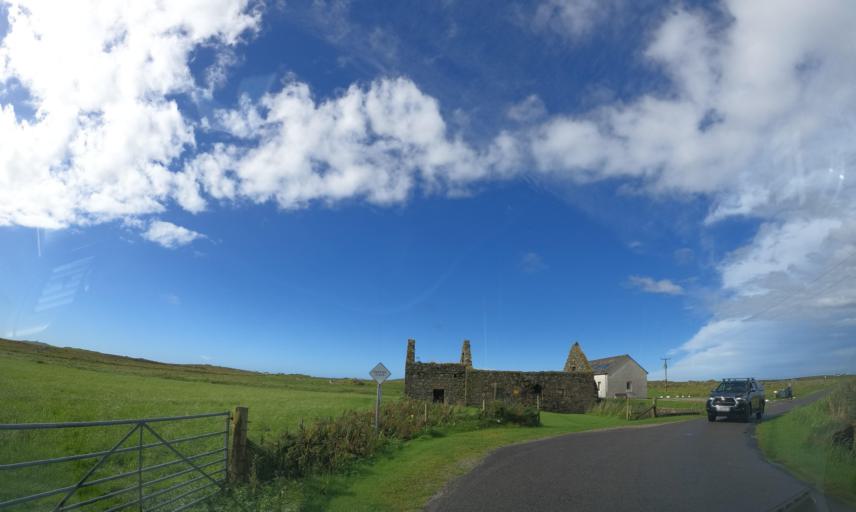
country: GB
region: Scotland
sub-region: Eilean Siar
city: Barra
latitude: 56.5199
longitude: -6.9146
